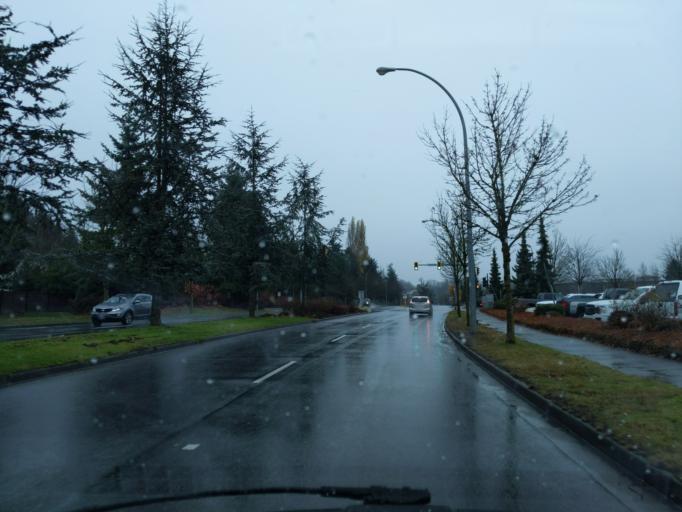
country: CA
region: British Columbia
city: Walnut Grove
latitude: 49.1694
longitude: -122.6628
